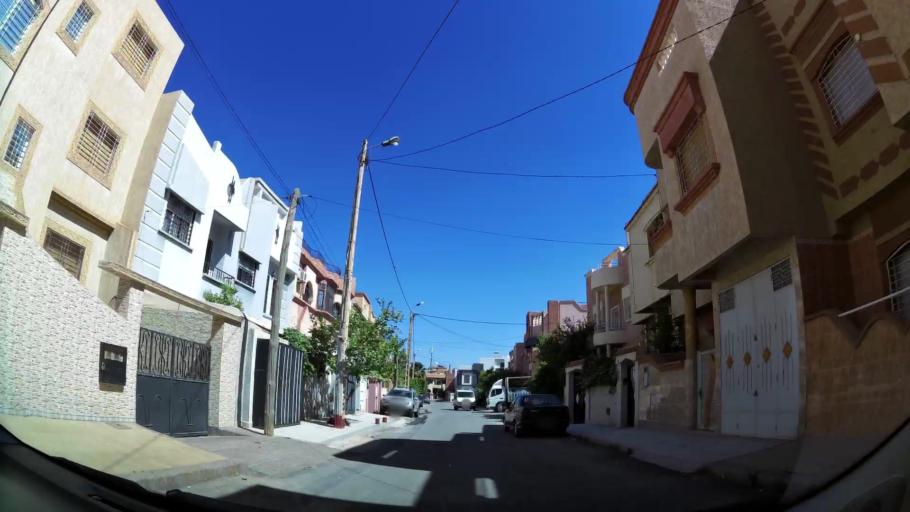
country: MA
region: Oriental
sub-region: Oujda-Angad
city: Oujda
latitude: 34.6627
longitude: -1.8947
